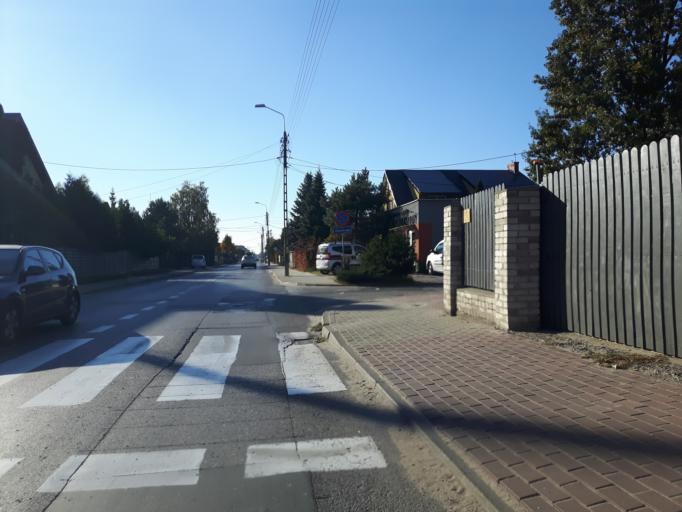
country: PL
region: Masovian Voivodeship
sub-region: Powiat wolominski
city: Zabki
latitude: 52.2852
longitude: 21.1335
